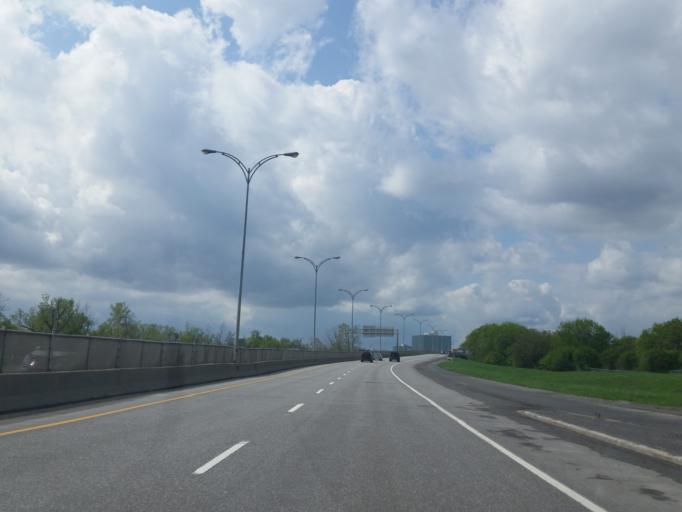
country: CA
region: Quebec
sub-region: Outaouais
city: Gatineau
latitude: 45.4443
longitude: -75.7223
